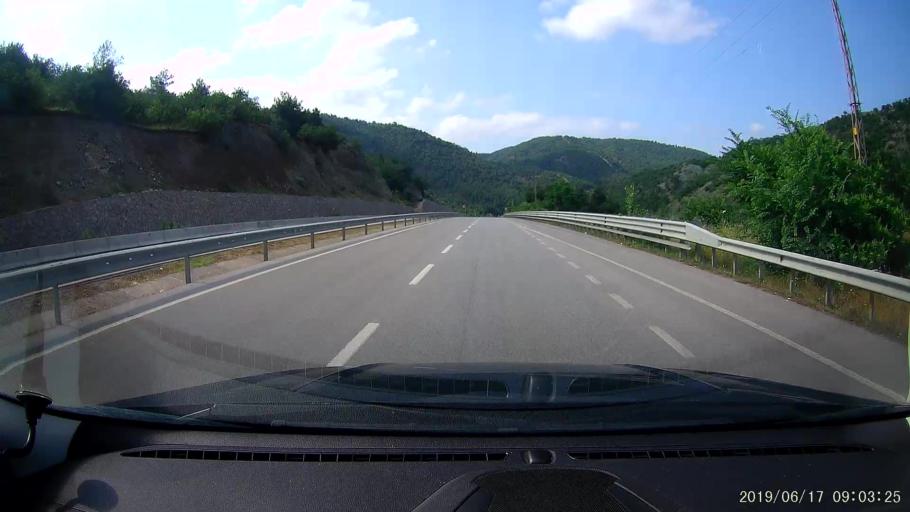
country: TR
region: Amasya
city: Tasova
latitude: 40.7558
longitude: 36.3023
